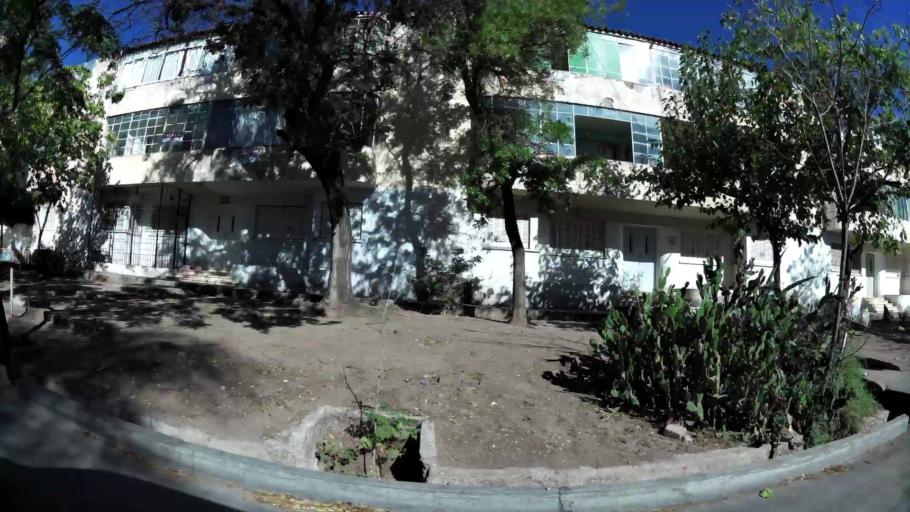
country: AR
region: Mendoza
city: Las Heras
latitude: -32.8690
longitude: -68.8598
